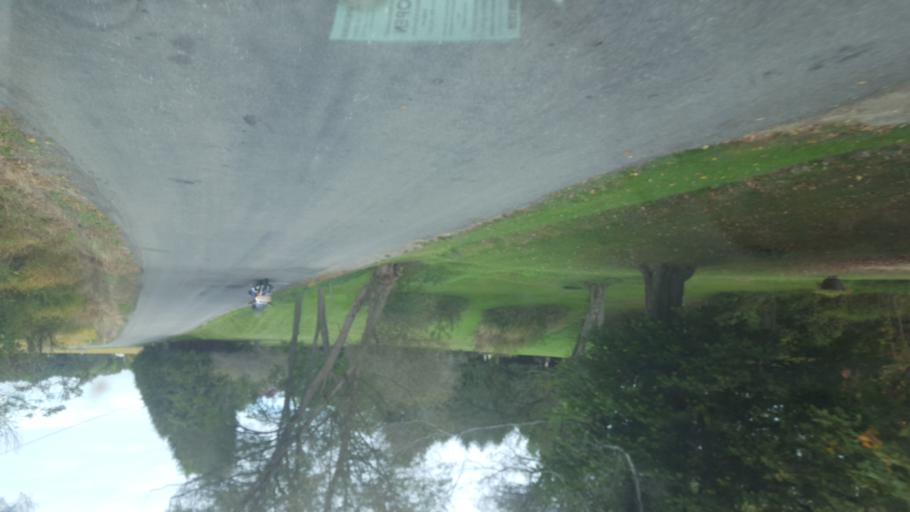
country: US
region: Pennsylvania
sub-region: Mercer County
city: Stoneboro
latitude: 41.3950
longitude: -80.2355
